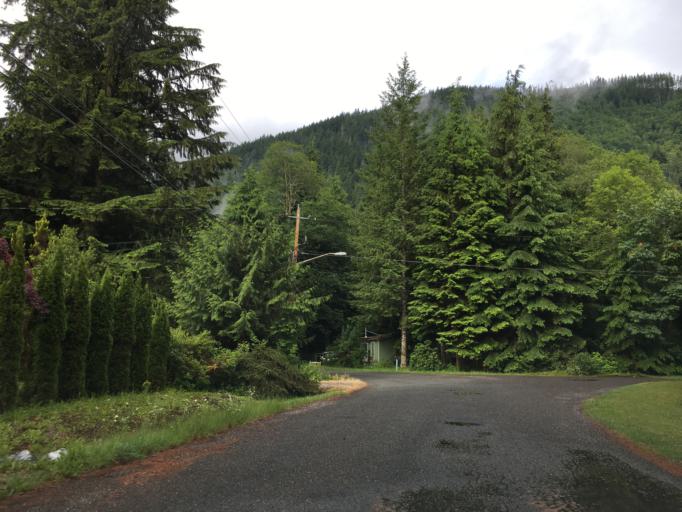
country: US
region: Washington
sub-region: Whatcom County
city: Peaceful Valley
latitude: 48.9314
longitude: -122.1494
